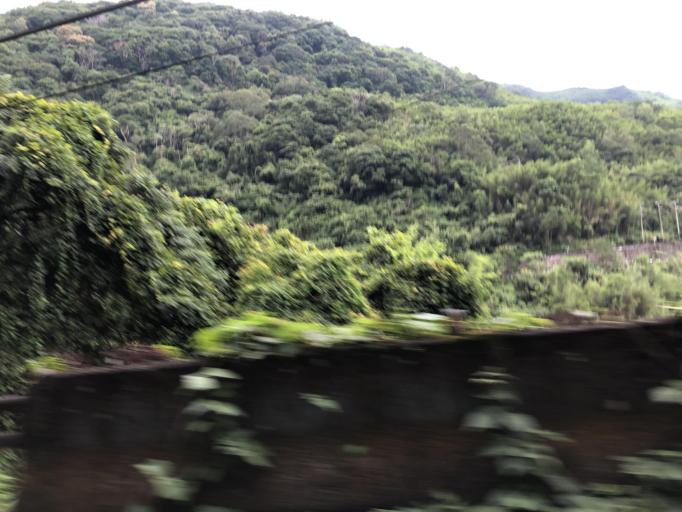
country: TW
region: Taiwan
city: Daxi
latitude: 24.7169
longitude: 121.3492
